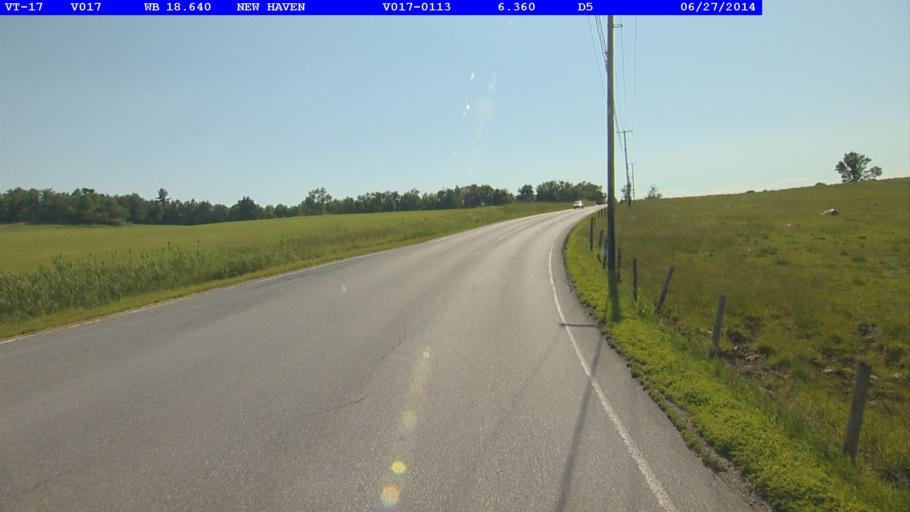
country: US
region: Vermont
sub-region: Addison County
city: Bristol
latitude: 44.1255
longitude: -73.1242
